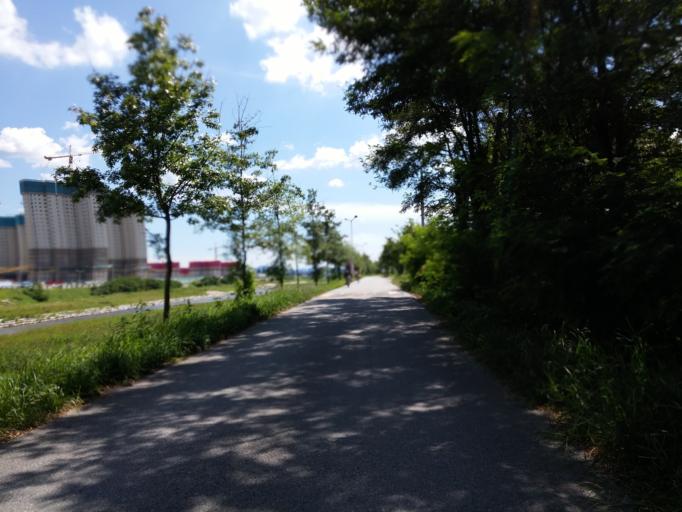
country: KR
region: Chungcheongbuk-do
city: Cheongju-si
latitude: 36.6044
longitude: 127.4973
